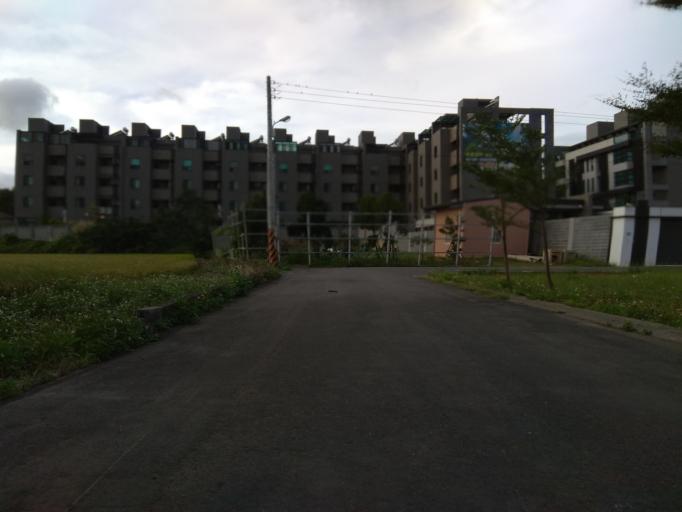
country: TW
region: Taiwan
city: Daxi
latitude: 24.9314
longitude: 121.1952
